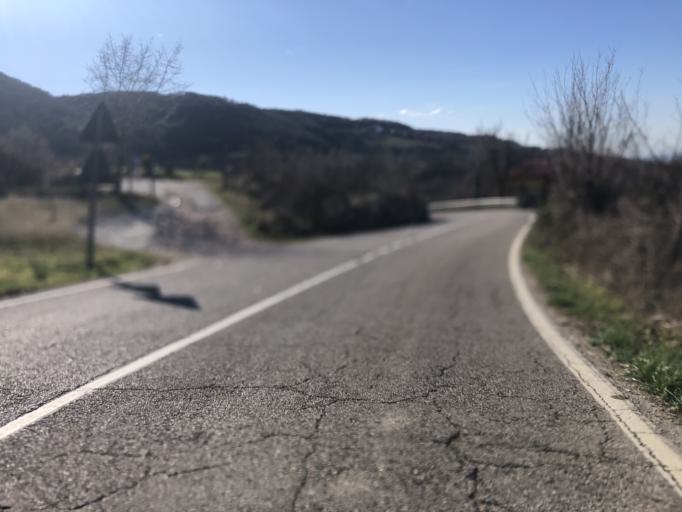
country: IT
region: Veneto
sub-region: Provincia di Verona
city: Dolce
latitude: 45.5626
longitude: 10.8493
